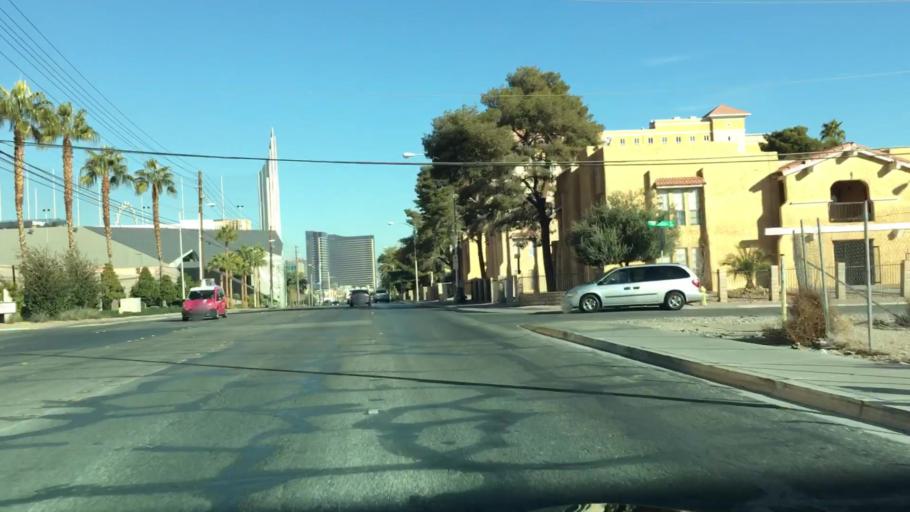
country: US
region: Nevada
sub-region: Clark County
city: Paradise
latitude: 36.1043
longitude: -115.1638
